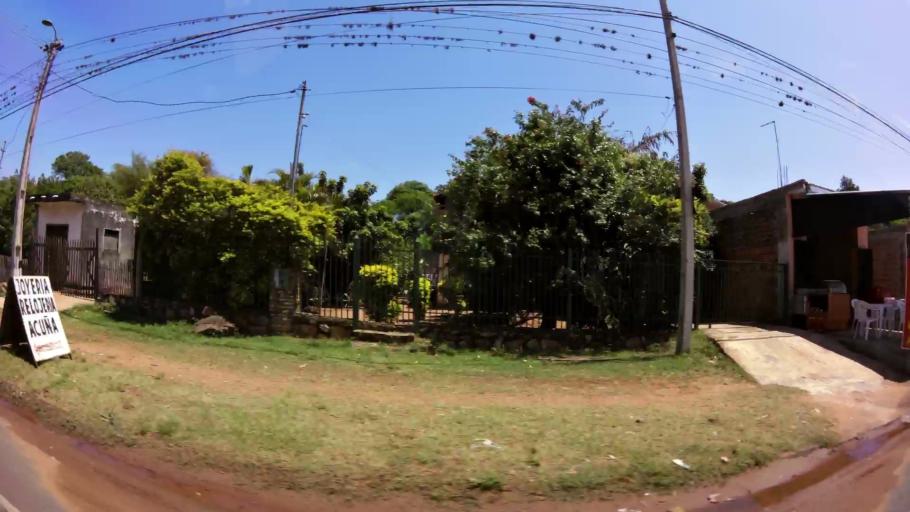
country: PY
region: Central
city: Nemby
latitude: -25.3863
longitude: -57.5236
